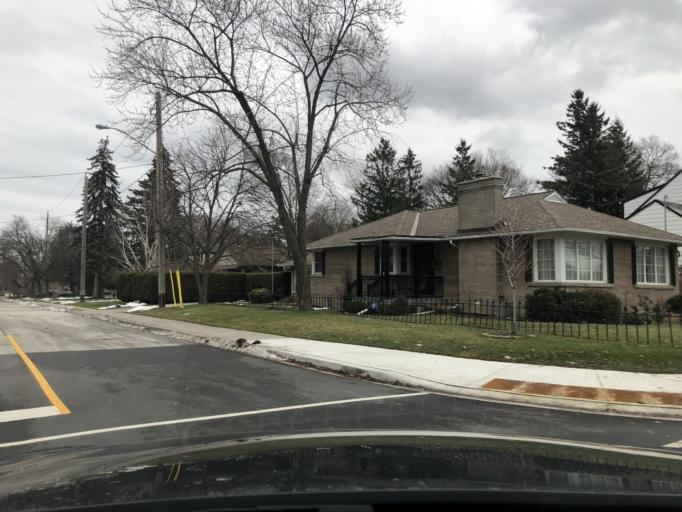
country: CA
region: Ontario
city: Etobicoke
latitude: 43.6987
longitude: -79.5335
